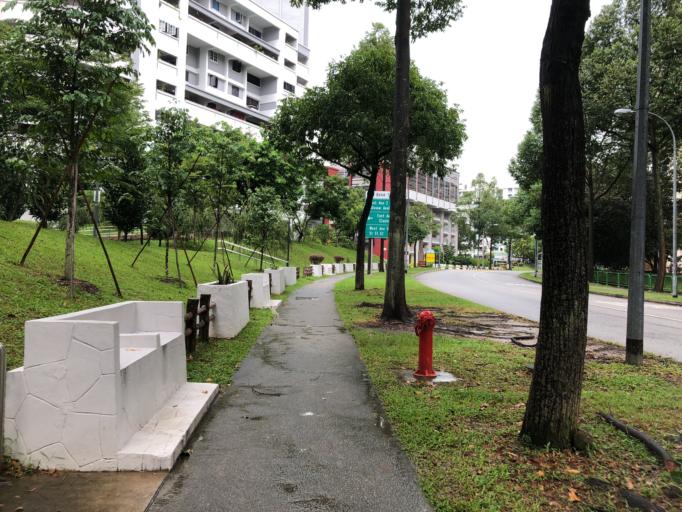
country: SG
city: Singapore
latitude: 1.3496
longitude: 103.7559
